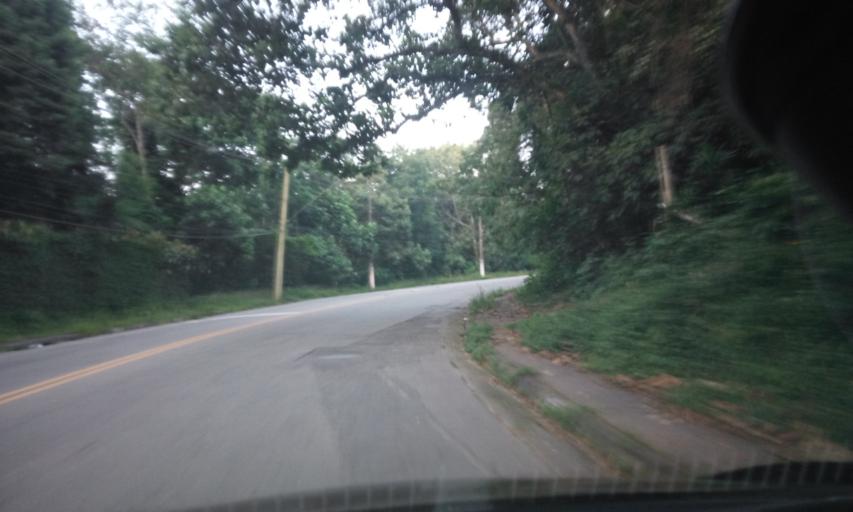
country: BR
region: Sao Paulo
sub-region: Sao Bernardo Do Campo
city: Sao Bernardo do Campo
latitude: -23.7951
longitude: -46.5412
